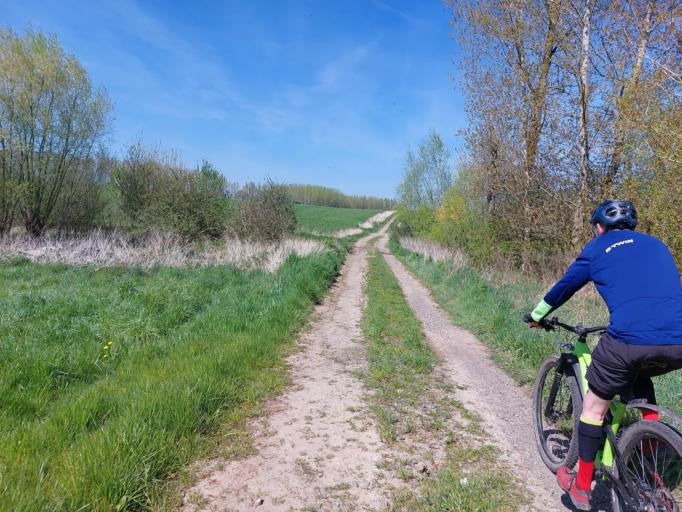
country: BE
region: Wallonia
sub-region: Province du Hainaut
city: Silly
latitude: 50.6015
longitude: 3.9752
